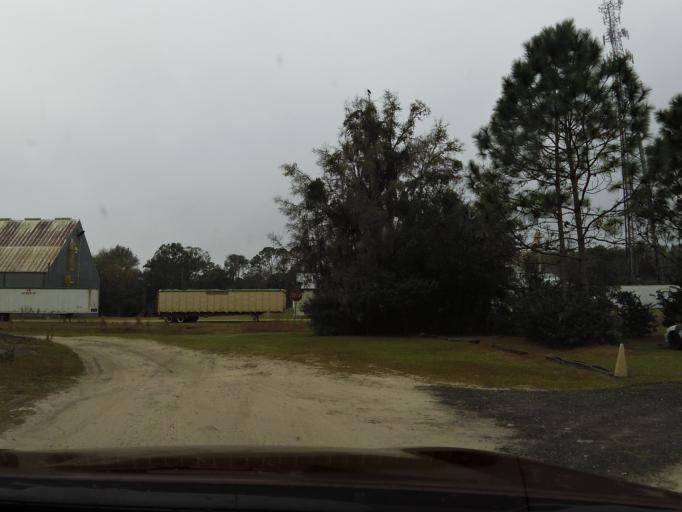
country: US
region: Florida
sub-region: Alachua County
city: High Springs
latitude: 29.8277
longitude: -82.6004
